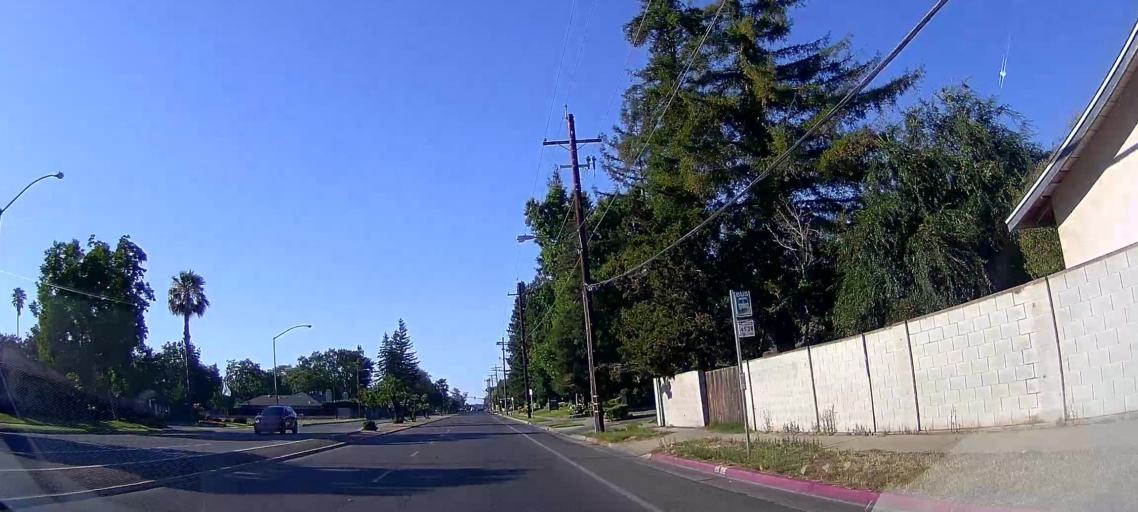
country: US
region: California
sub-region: Fresno County
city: Fresno
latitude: 36.8273
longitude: -119.8083
